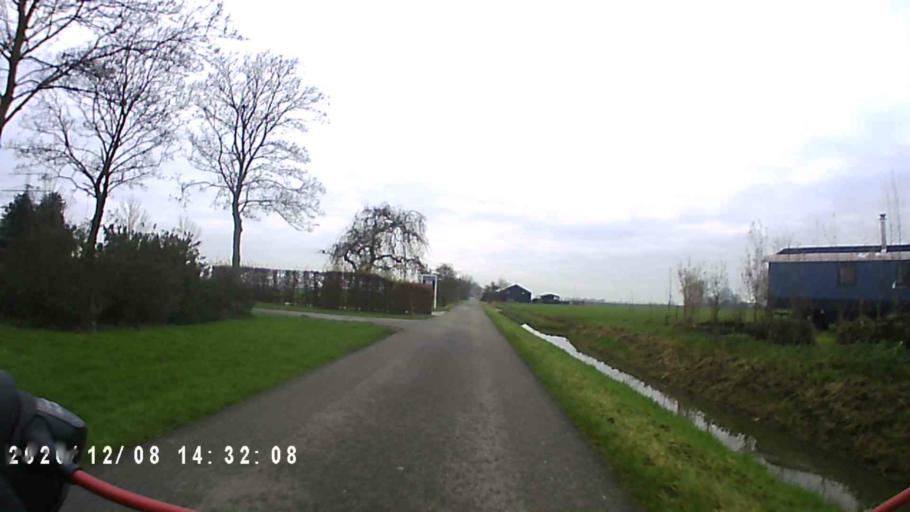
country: NL
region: Groningen
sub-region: Gemeente Winsum
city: Winsum
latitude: 53.2975
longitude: 6.5362
